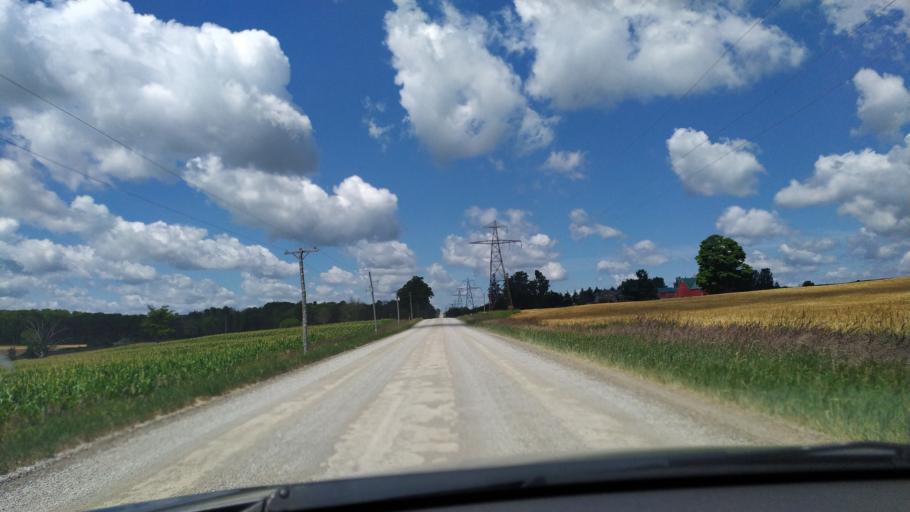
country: CA
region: Ontario
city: Stratford
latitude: 43.3875
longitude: -80.7845
